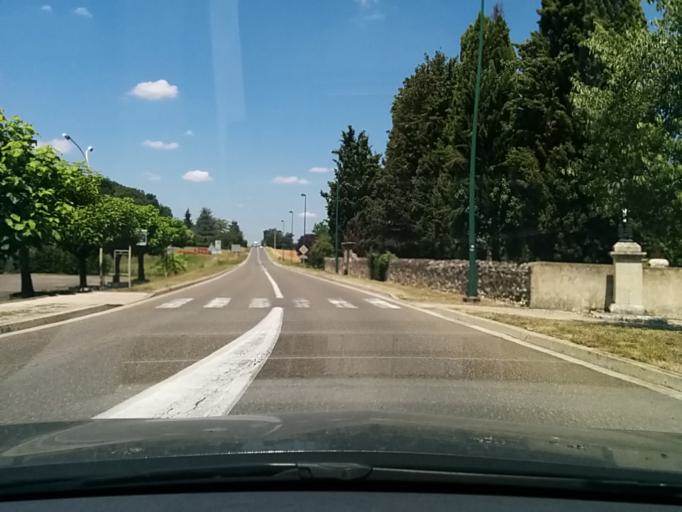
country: FR
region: Midi-Pyrenees
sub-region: Departement du Gers
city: Vic-Fezensac
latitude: 43.7264
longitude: 0.3757
